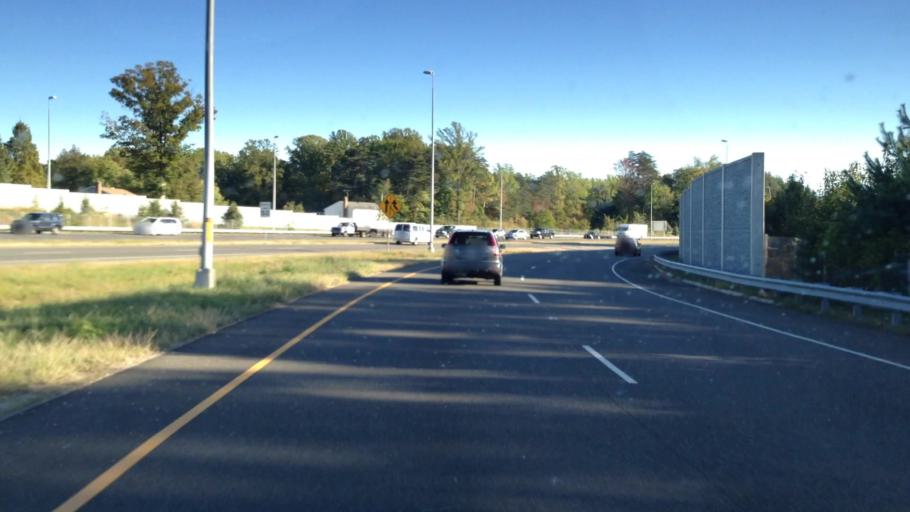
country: US
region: Virginia
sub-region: Fairfax County
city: West Springfield
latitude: 38.7578
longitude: -77.2163
